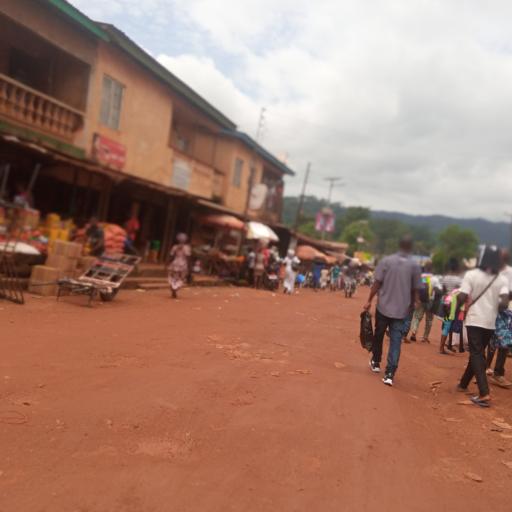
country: SL
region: Eastern Province
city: Kenema
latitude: 7.8757
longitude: -11.1933
